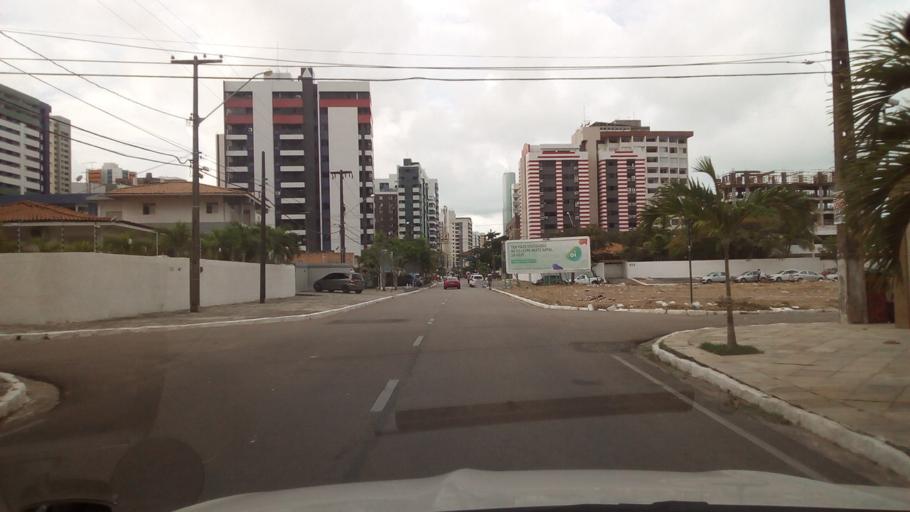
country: BR
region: Paraiba
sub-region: Joao Pessoa
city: Joao Pessoa
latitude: -7.1218
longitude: -34.8277
